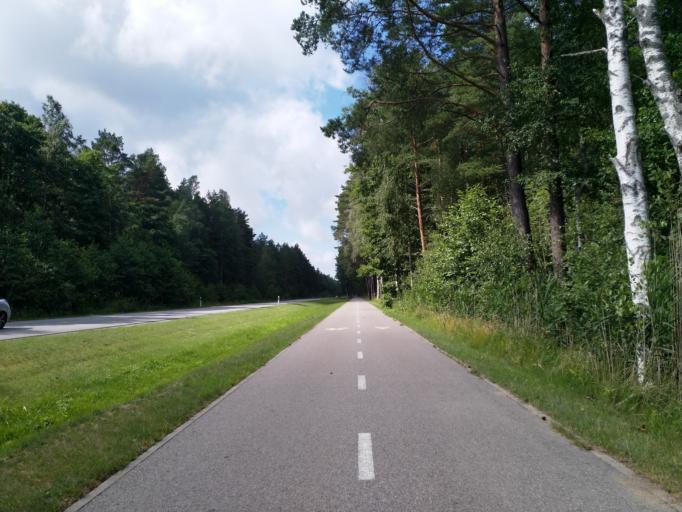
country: LV
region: Ventspils
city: Ventspils
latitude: 57.4289
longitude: 21.6477
